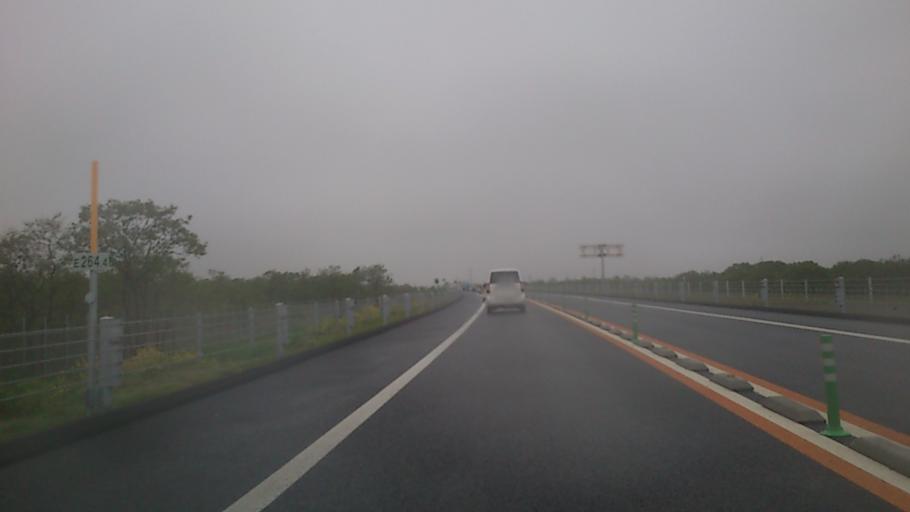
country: JP
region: Hokkaido
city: Kushiro
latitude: 43.0319
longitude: 144.3954
